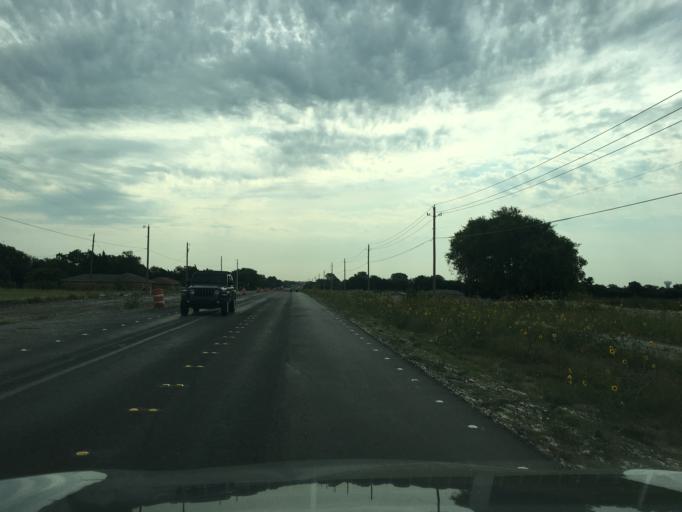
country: US
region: Texas
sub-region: Collin County
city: Parker
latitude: 33.0553
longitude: -96.6071
